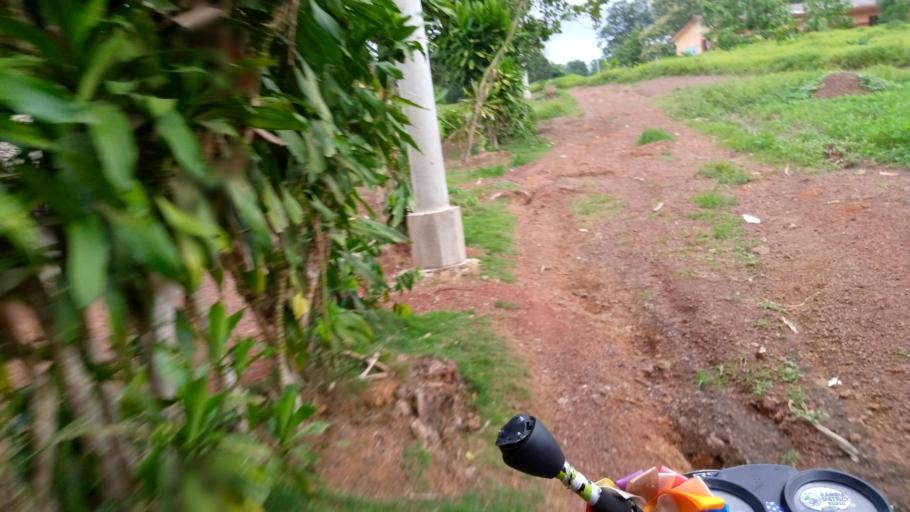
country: SL
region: Southern Province
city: Moyamba
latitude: 8.1651
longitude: -12.4418
